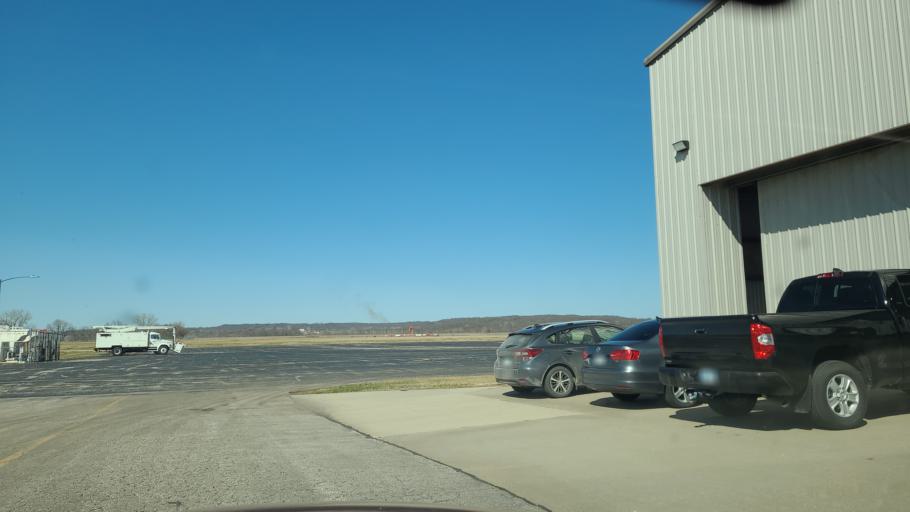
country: US
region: Kansas
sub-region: Douglas County
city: Lawrence
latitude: 39.0052
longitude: -95.2179
